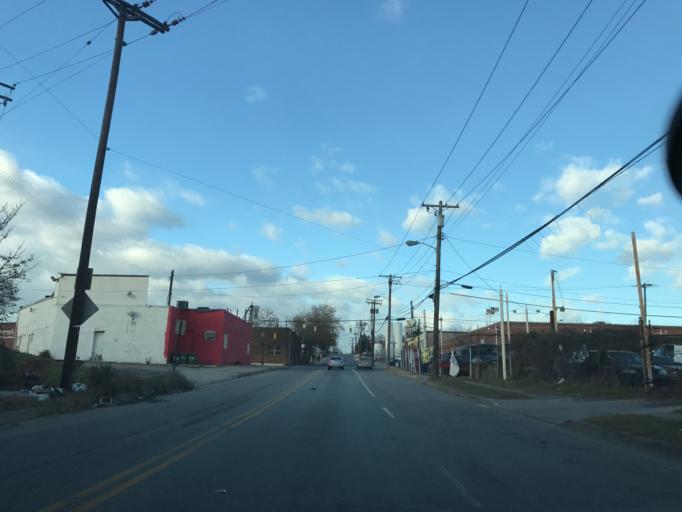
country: US
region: Maryland
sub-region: Baltimore County
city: Rosedale
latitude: 39.2989
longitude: -76.5603
